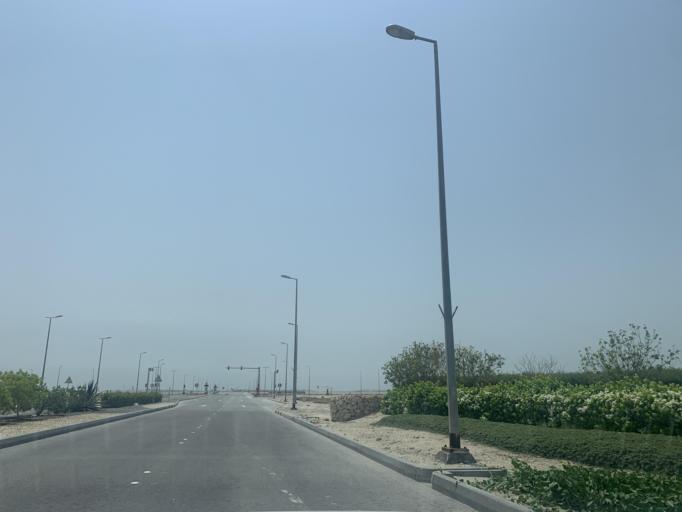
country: BH
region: Central Governorate
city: Dar Kulayb
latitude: 25.8469
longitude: 50.5942
